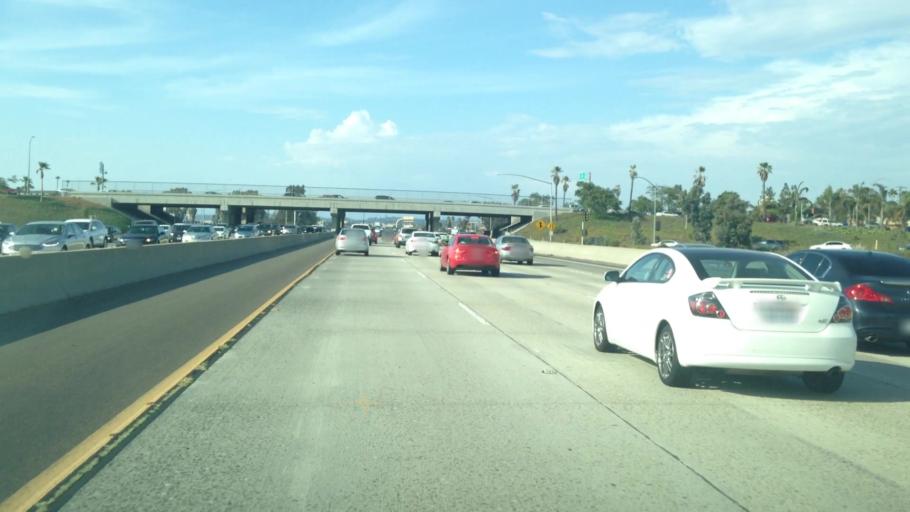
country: US
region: California
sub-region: San Diego County
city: San Diego
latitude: 32.8307
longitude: -117.1418
